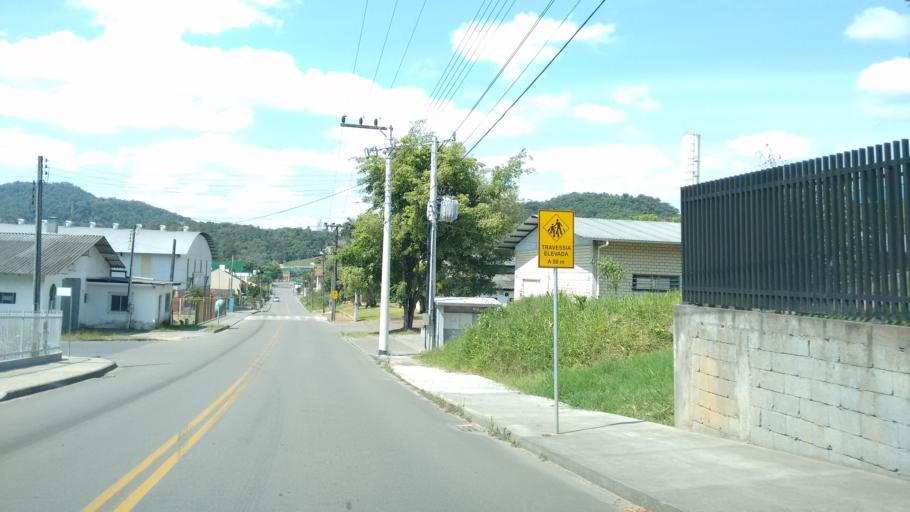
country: BR
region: Santa Catarina
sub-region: Pomerode
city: Pomerode
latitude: -26.7178
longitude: -49.1749
